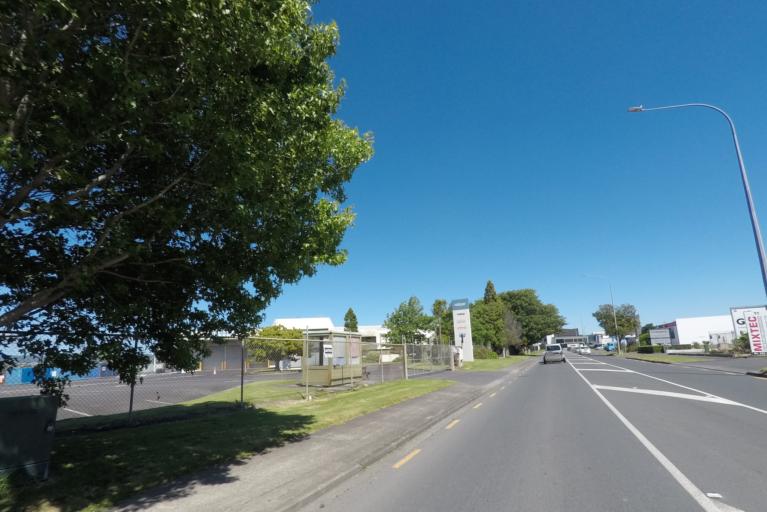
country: NZ
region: Auckland
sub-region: Auckland
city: Rosebank
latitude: -36.8722
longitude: 174.6686
